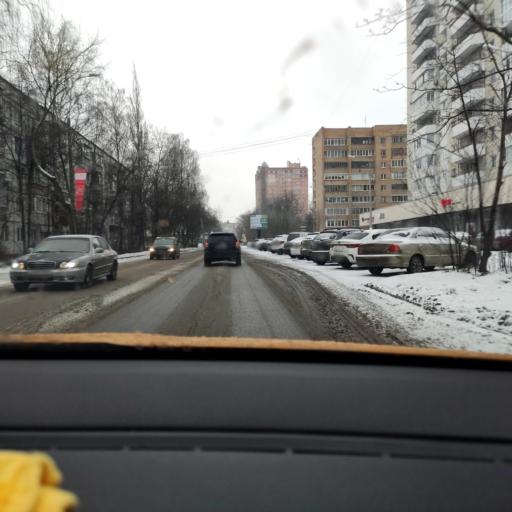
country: RU
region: Moskovskaya
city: Ivanteyevka
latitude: 55.9675
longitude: 37.8971
